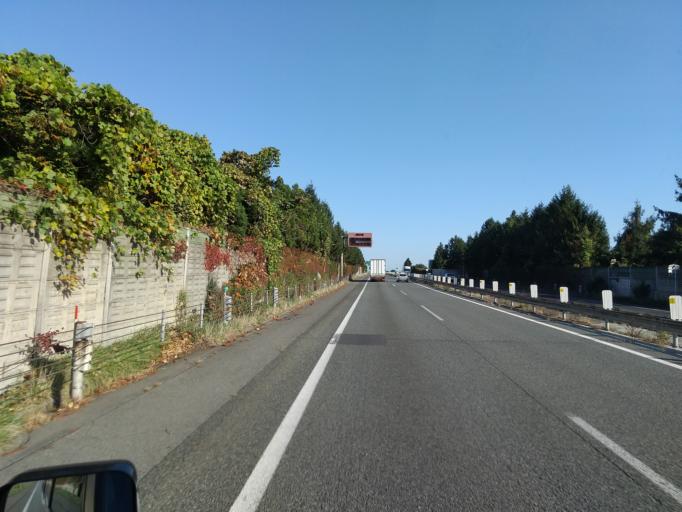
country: JP
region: Iwate
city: Kitakami
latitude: 39.2922
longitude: 141.0847
